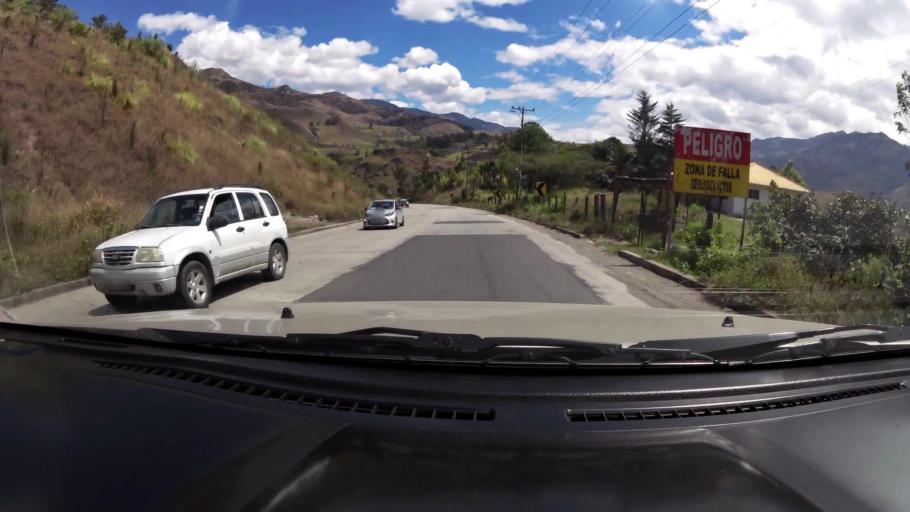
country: EC
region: Azuay
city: Cuenca
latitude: -3.1976
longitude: -79.1806
